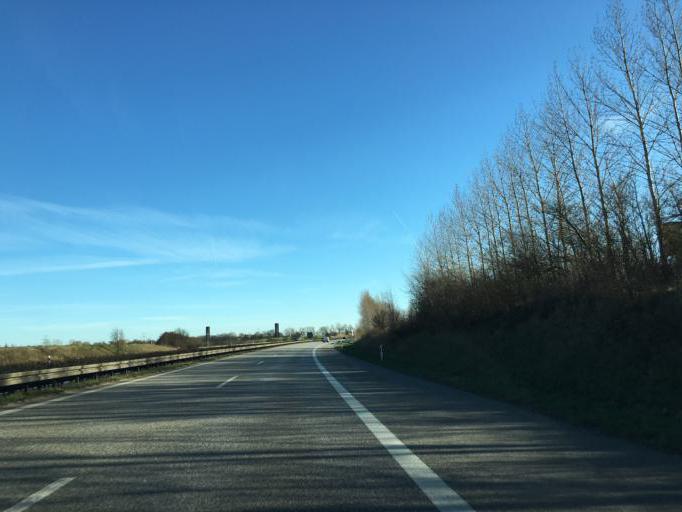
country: DE
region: Mecklenburg-Vorpommern
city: Bentwisch
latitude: 54.0990
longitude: 12.1997
